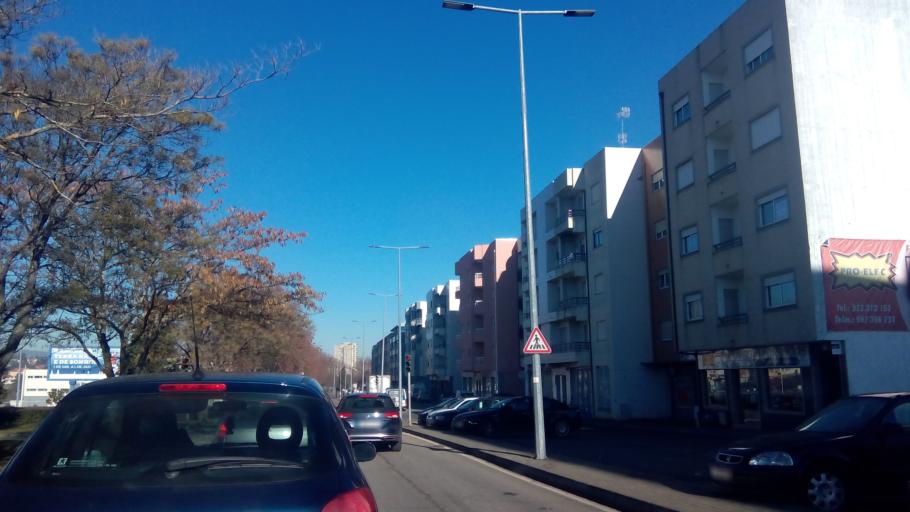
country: PT
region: Braganca
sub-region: Braganca Municipality
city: Braganca
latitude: 41.7914
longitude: -6.7702
